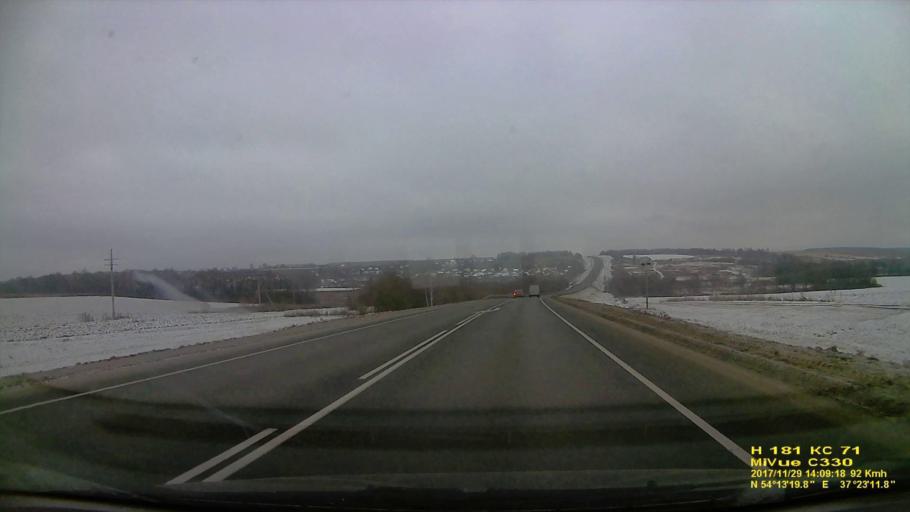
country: RU
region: Tula
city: Leninskiy
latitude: 54.2220
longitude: 37.3869
